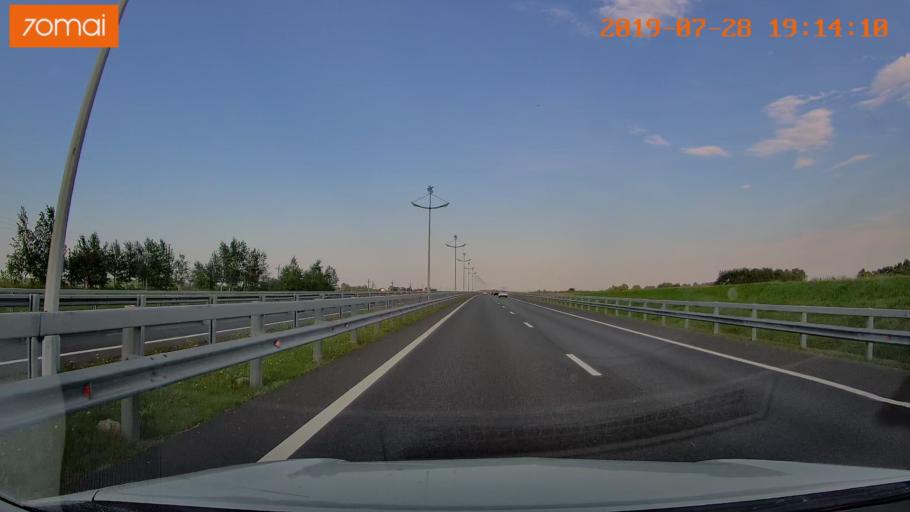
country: RU
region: Kaliningrad
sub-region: Gorod Kaliningrad
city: Pionerskiy
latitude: 54.9214
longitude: 20.3114
